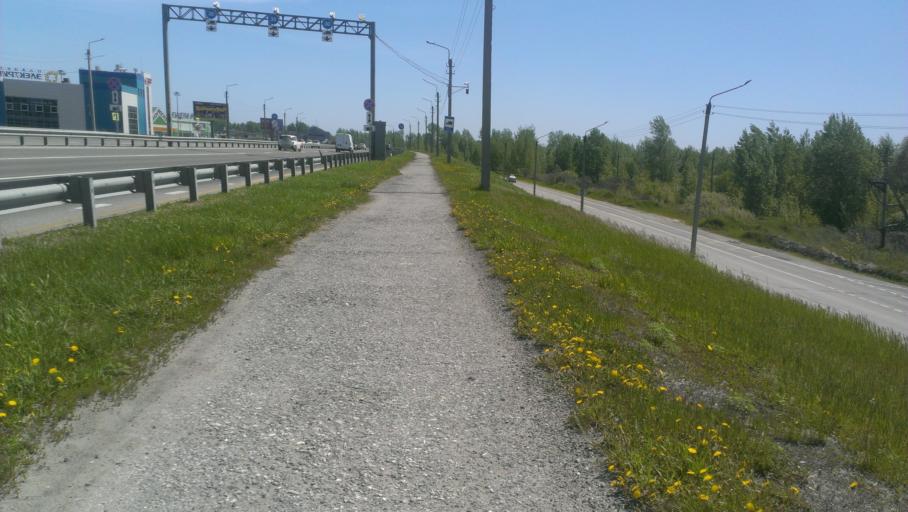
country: RU
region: Altai Krai
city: Zaton
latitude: 53.3169
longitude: 83.8223
